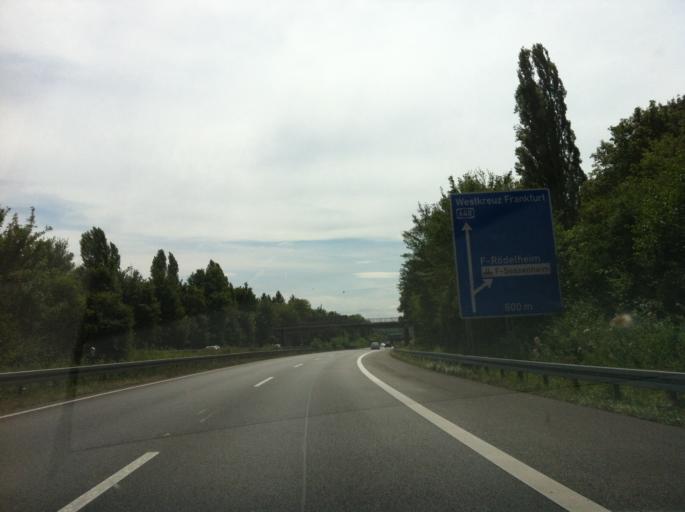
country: DE
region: Hesse
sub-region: Regierungsbezirk Darmstadt
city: Eschborn
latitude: 50.1273
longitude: 8.5761
